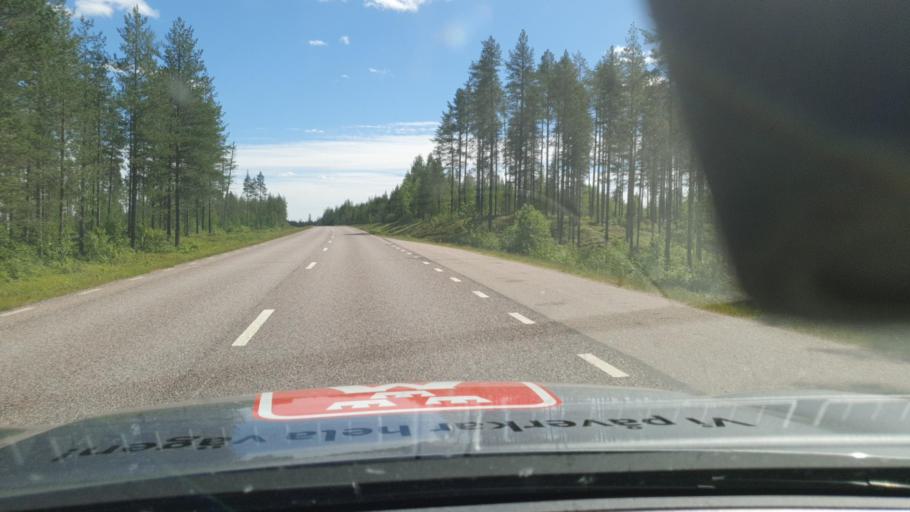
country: FI
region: Lapland
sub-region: Tunturi-Lappi
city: Kolari
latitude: 67.0449
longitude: 23.6855
